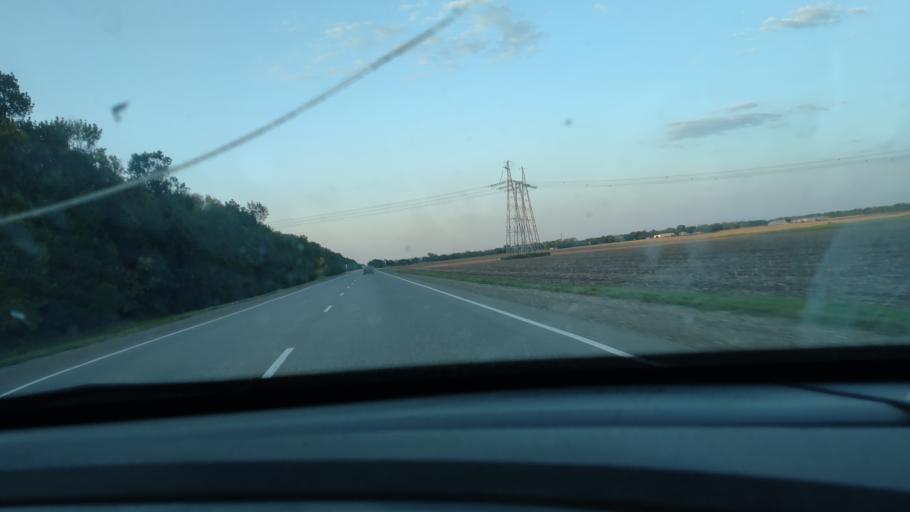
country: RU
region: Krasnodarskiy
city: Novominskaya
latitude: 46.4003
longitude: 38.9966
